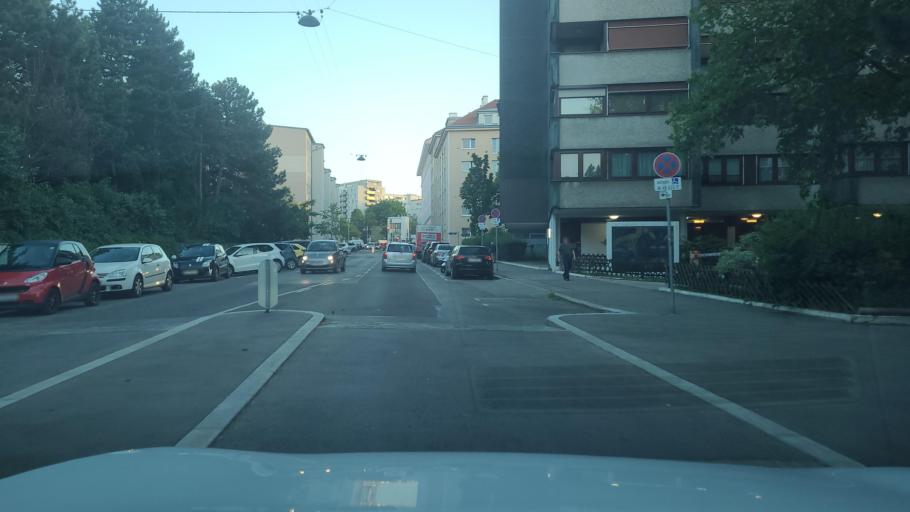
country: AT
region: Vienna
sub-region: Wien Stadt
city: Vienna
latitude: 48.1730
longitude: 16.3580
